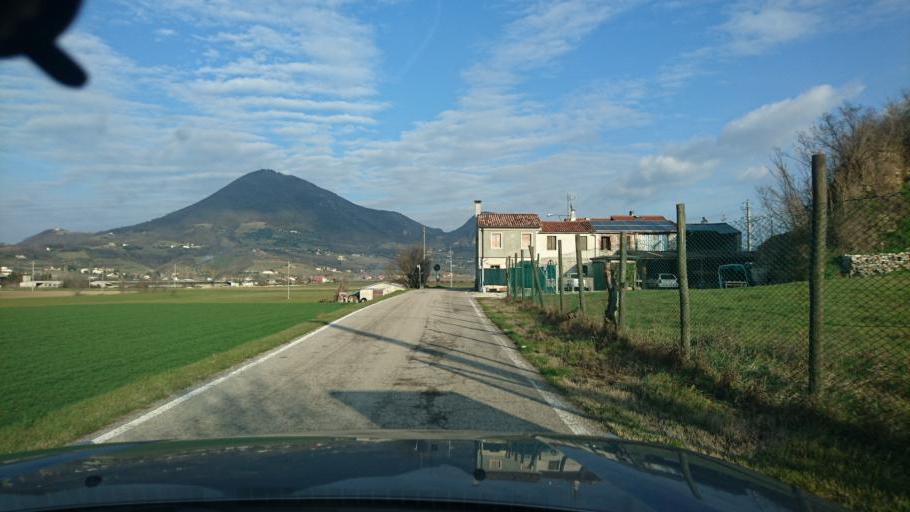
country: IT
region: Veneto
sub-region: Provincia di Padova
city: Vo
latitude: 45.3471
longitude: 11.6215
